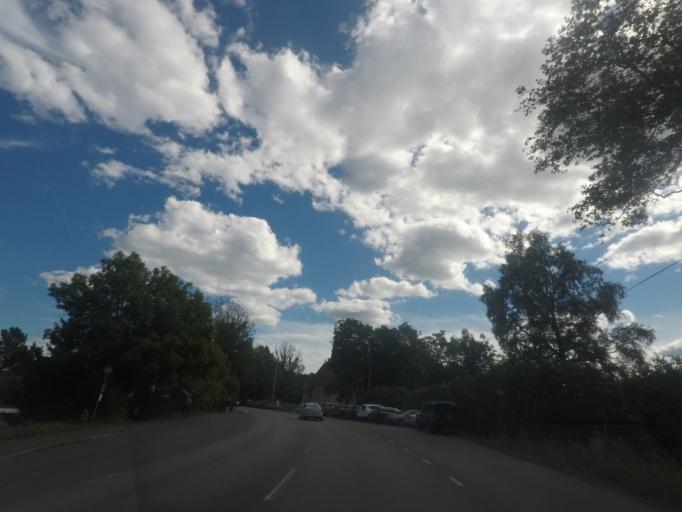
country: SE
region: Stockholm
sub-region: Norrtalje Kommun
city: Arno
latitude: 60.0987
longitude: 18.8100
